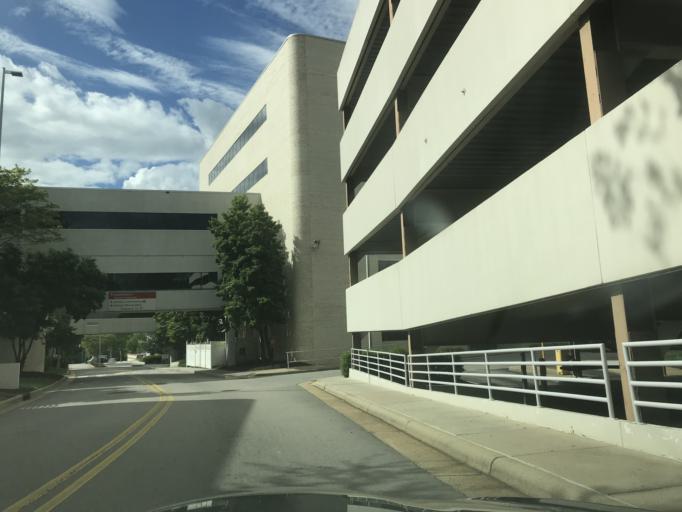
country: US
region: North Carolina
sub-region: Wake County
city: Raleigh
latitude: 35.7852
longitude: -78.5870
